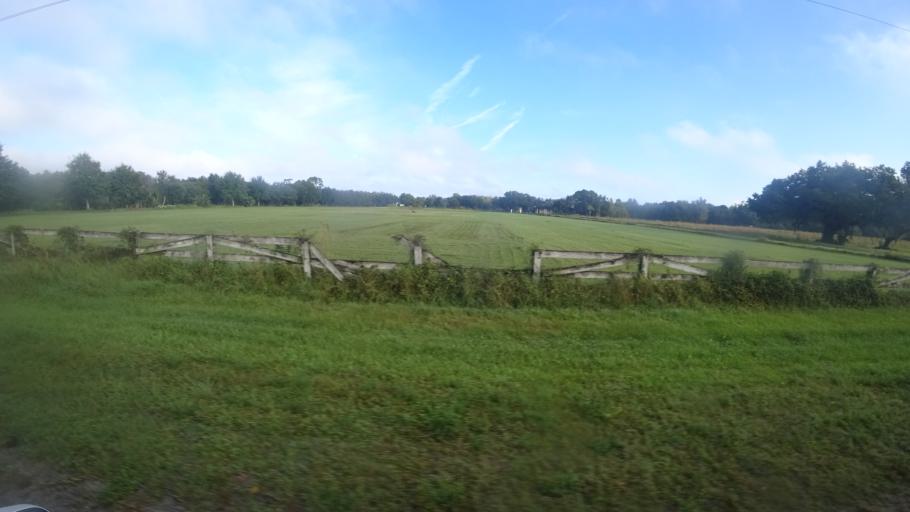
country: US
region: Florida
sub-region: Manatee County
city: Ellenton
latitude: 27.5354
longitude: -82.4705
